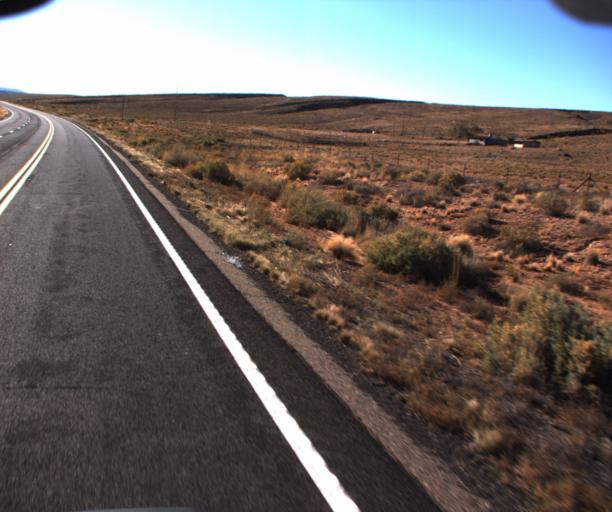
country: US
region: Arizona
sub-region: Coconino County
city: LeChee
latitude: 36.5615
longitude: -111.6357
